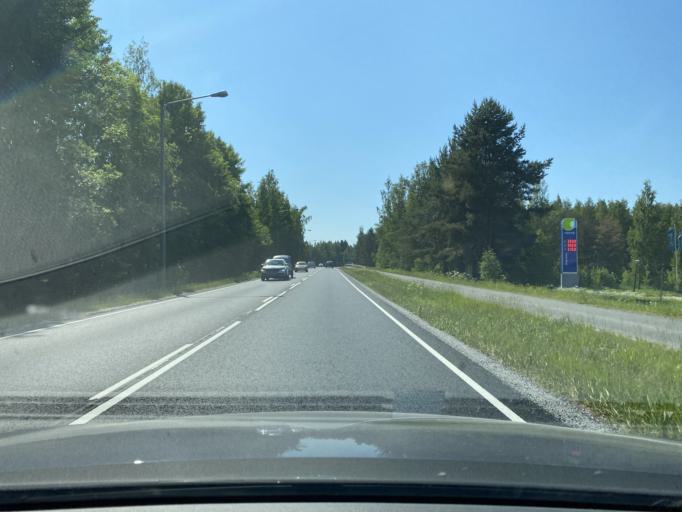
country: FI
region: Pirkanmaa
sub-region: Tampere
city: Nokia
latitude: 61.4647
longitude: 23.5075
